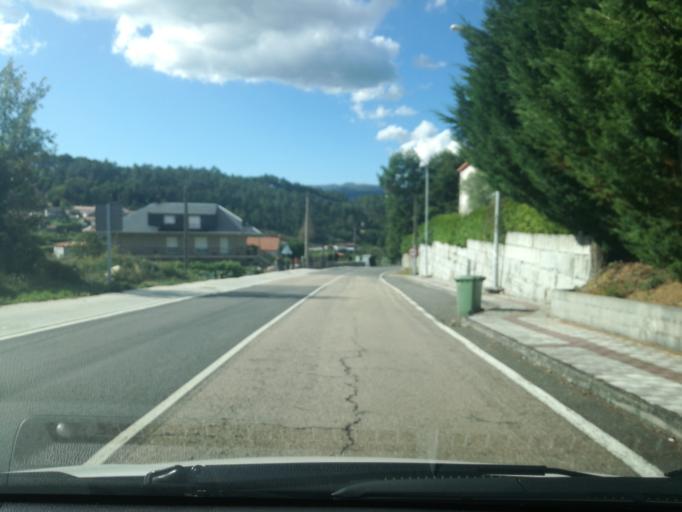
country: ES
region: Galicia
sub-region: Provincia de Ourense
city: Lobios
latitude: 41.8956
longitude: -8.0849
